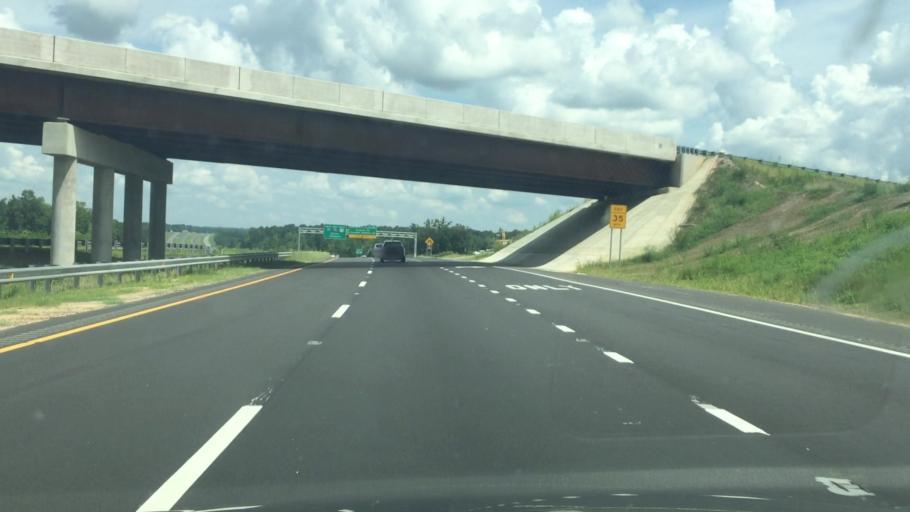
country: US
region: North Carolina
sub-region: Richmond County
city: Ellerbe
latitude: 35.0112
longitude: -79.7708
